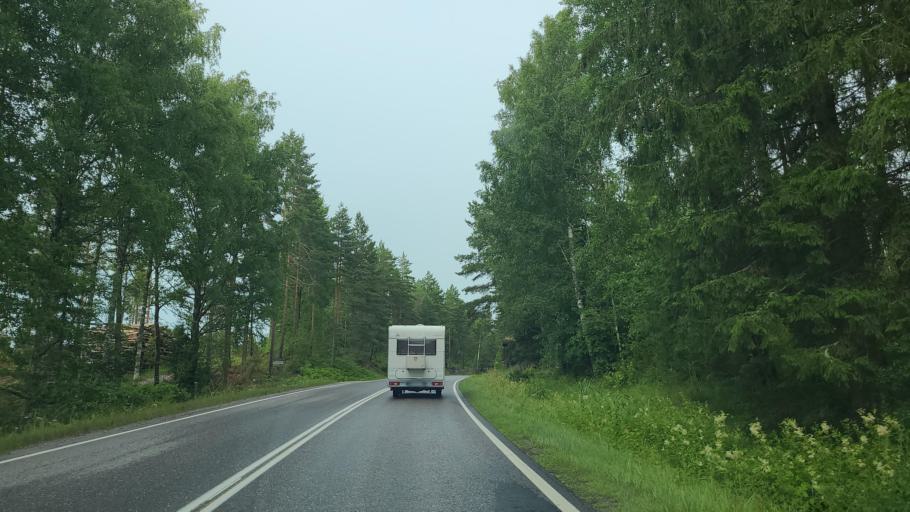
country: FI
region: Varsinais-Suomi
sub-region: Turku
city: Sauvo
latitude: 60.3019
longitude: 22.6812
